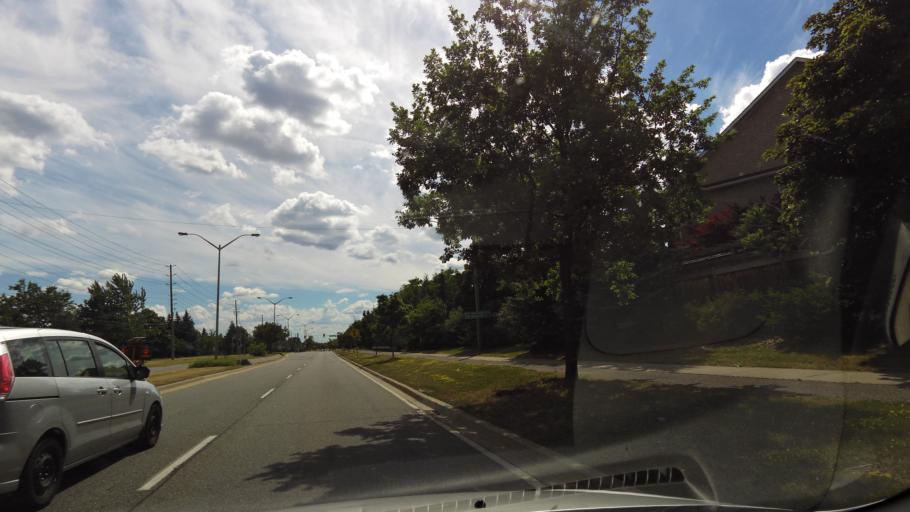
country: CA
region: Ontario
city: Oakville
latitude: 43.4738
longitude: -79.7032
